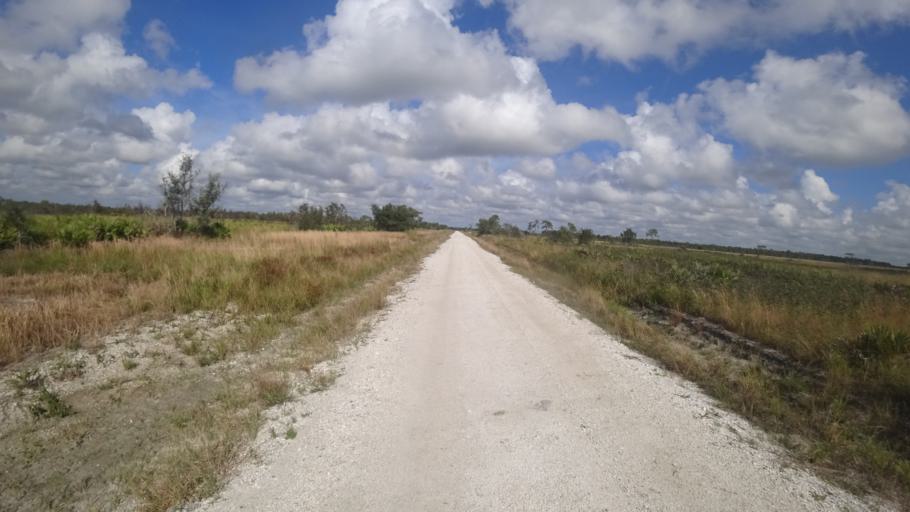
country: US
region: Florida
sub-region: Hillsborough County
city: Wimauma
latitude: 27.5263
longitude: -82.1277
